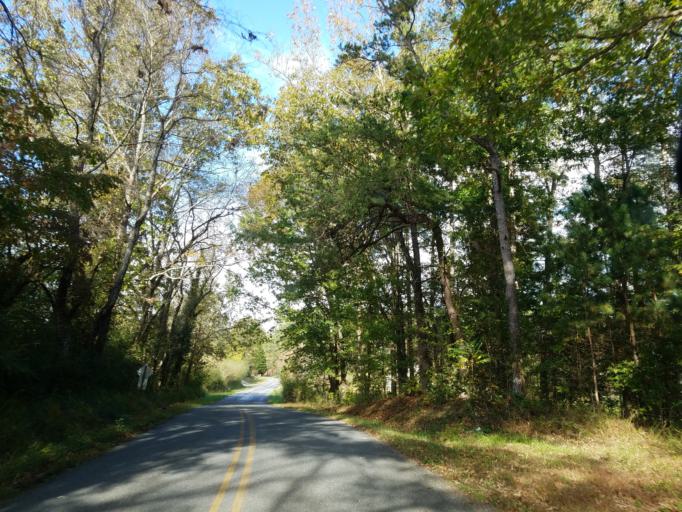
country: US
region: Georgia
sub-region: Gilmer County
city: Ellijay
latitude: 34.6308
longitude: -84.3742
